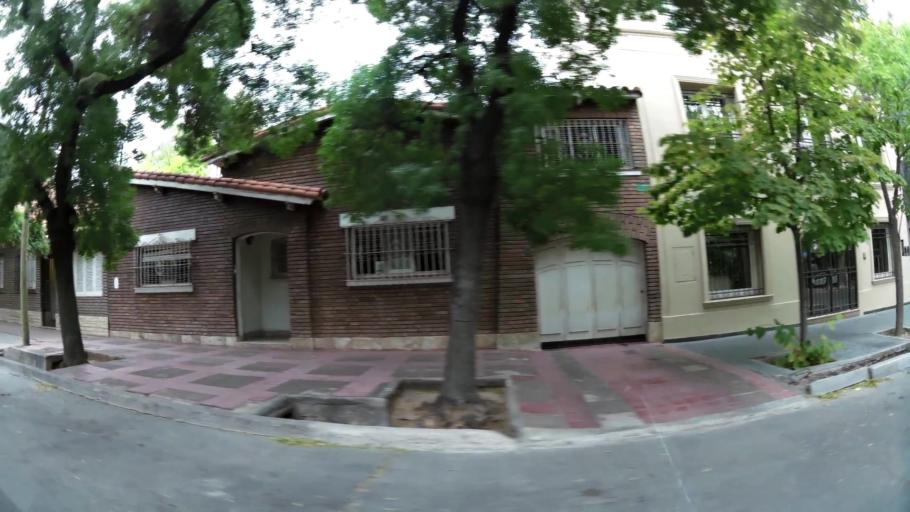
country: AR
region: Mendoza
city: Mendoza
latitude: -32.8798
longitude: -68.8571
